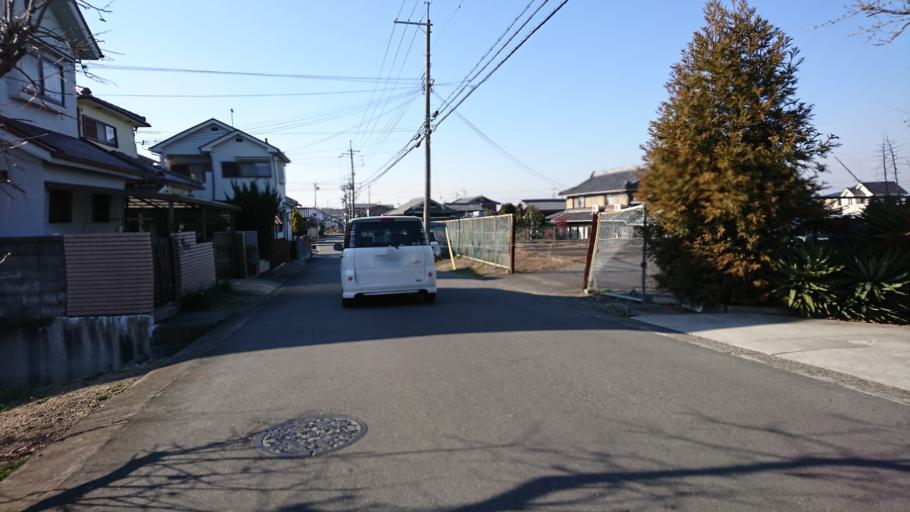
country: JP
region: Hyogo
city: Kakogawacho-honmachi
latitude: 34.7782
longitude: 134.8784
